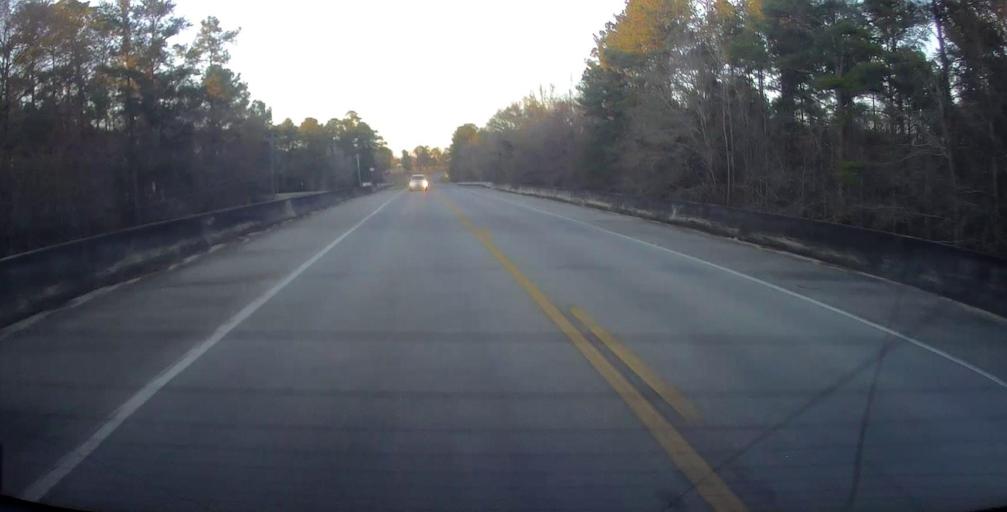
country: US
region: Georgia
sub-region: Dodge County
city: Eastman
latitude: 32.2544
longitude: -83.1403
